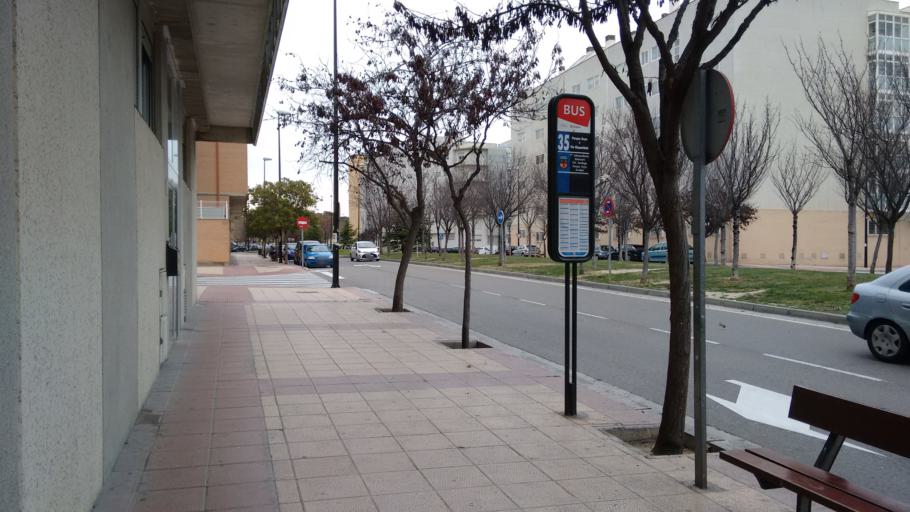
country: ES
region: Aragon
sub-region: Provincia de Zaragoza
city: Zaragoza
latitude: 41.6871
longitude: -0.8778
